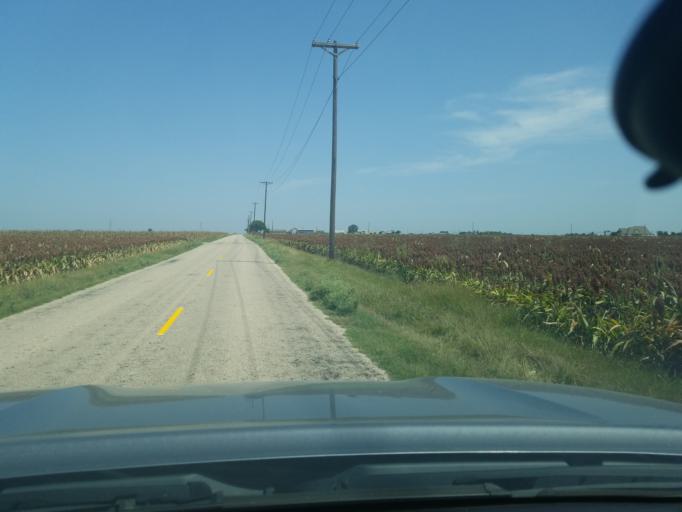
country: US
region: Texas
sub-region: Guadalupe County
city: Lake Dunlap
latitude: 29.6845
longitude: -98.0327
